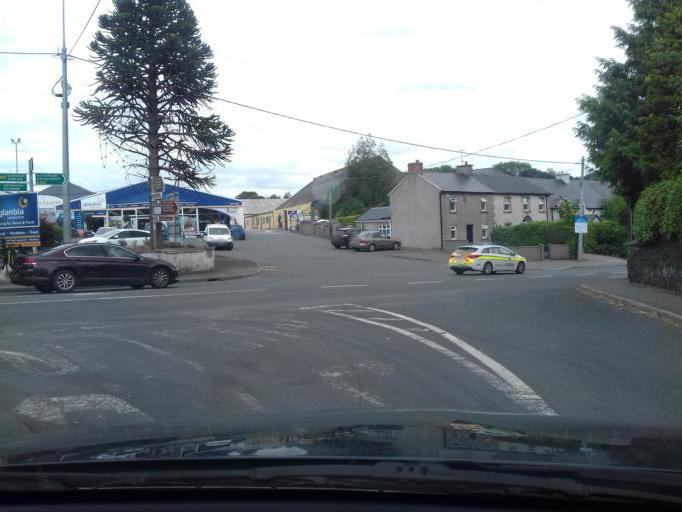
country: IE
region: Leinster
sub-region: Loch Garman
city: Bunclody
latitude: 52.6561
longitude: -6.6587
